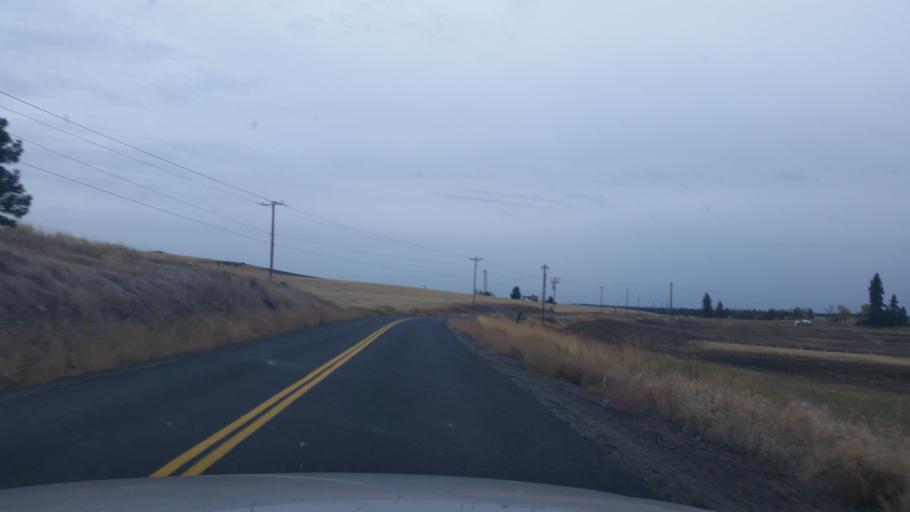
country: US
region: Washington
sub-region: Spokane County
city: Cheney
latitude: 47.5323
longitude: -117.5510
